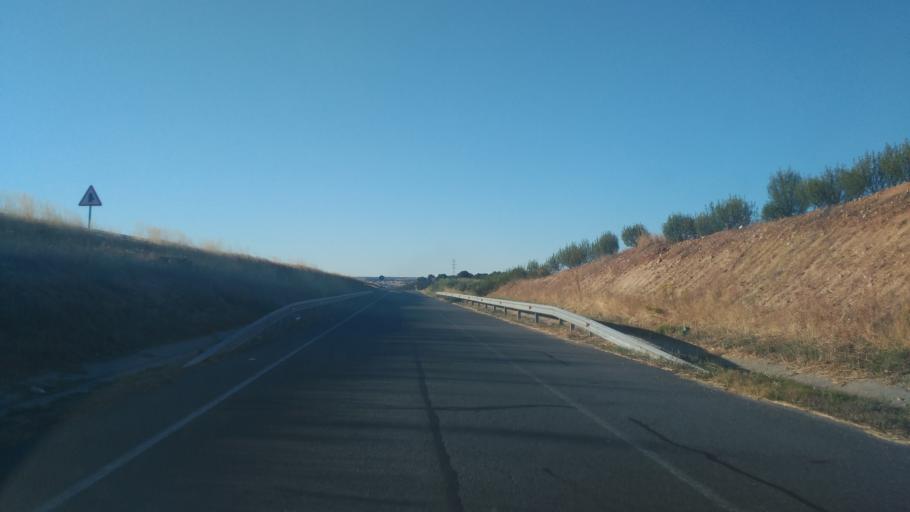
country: ES
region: Castille and Leon
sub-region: Provincia de Salamanca
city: Montejo
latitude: 40.6707
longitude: -5.6179
